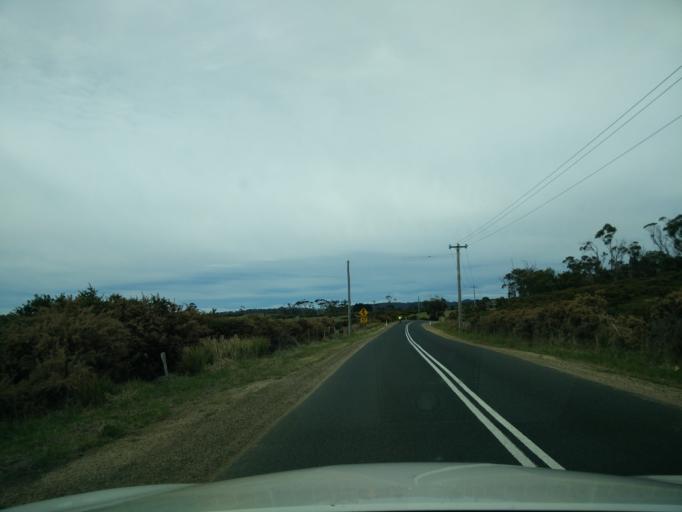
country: AU
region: Tasmania
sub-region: Break O'Day
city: St Helens
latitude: -41.9254
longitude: 148.2369
